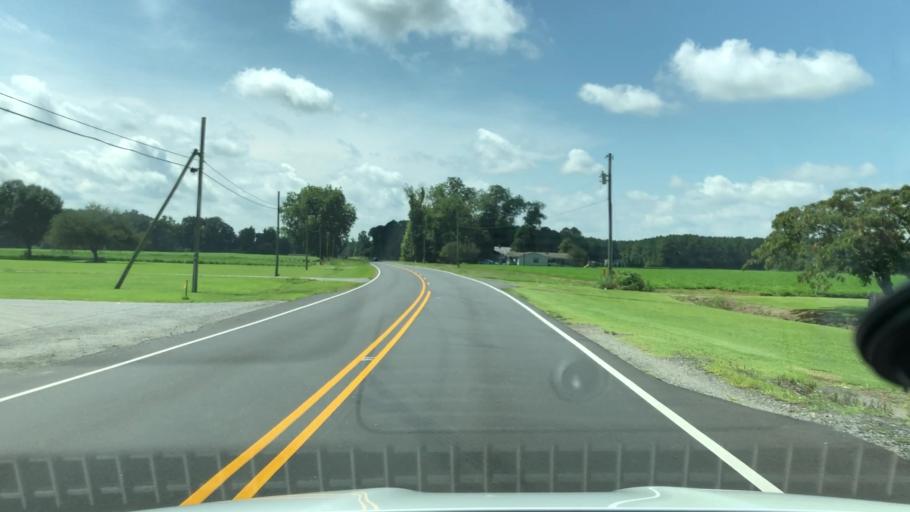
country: US
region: North Carolina
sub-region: Martin County
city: Williamston
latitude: 35.7634
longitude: -77.0745
